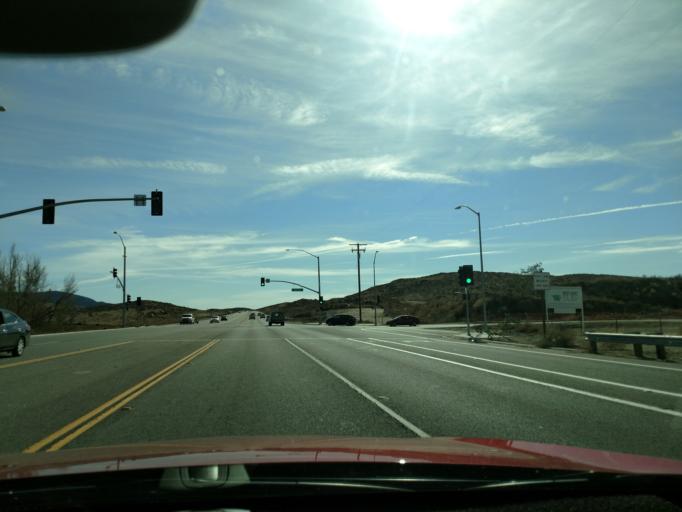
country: US
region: California
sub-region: Riverside County
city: Winchester
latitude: 33.6574
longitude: -117.0846
